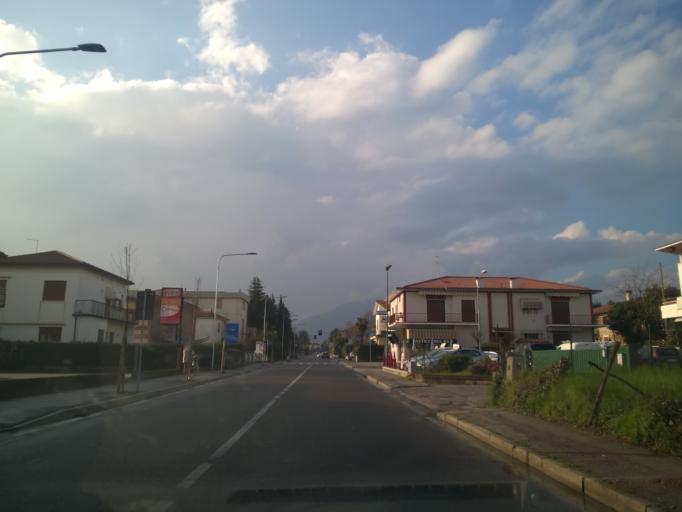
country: IT
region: Veneto
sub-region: Provincia di Vicenza
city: Thiene
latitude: 45.7052
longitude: 11.4726
